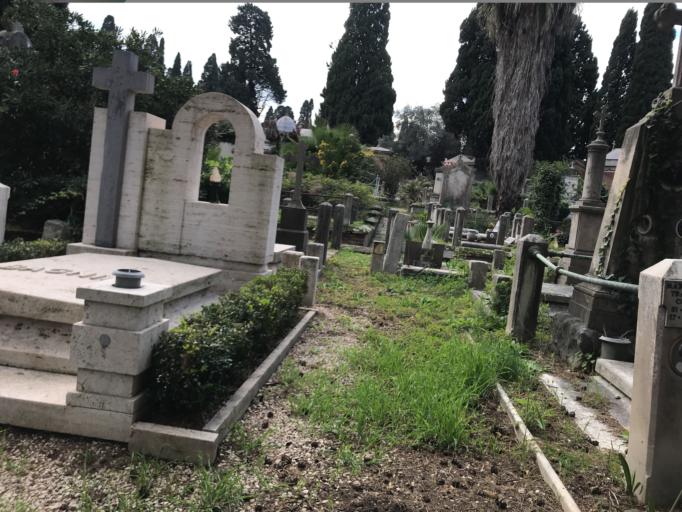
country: IT
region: Latium
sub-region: Citta metropolitana di Roma Capitale
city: Rome
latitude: 41.9050
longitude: 12.5228
